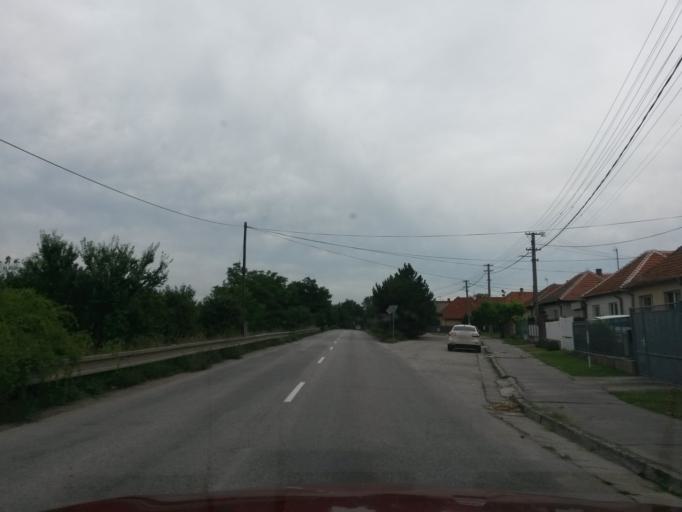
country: SK
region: Nitriansky
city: Surany
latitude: 48.1121
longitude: 18.2399
